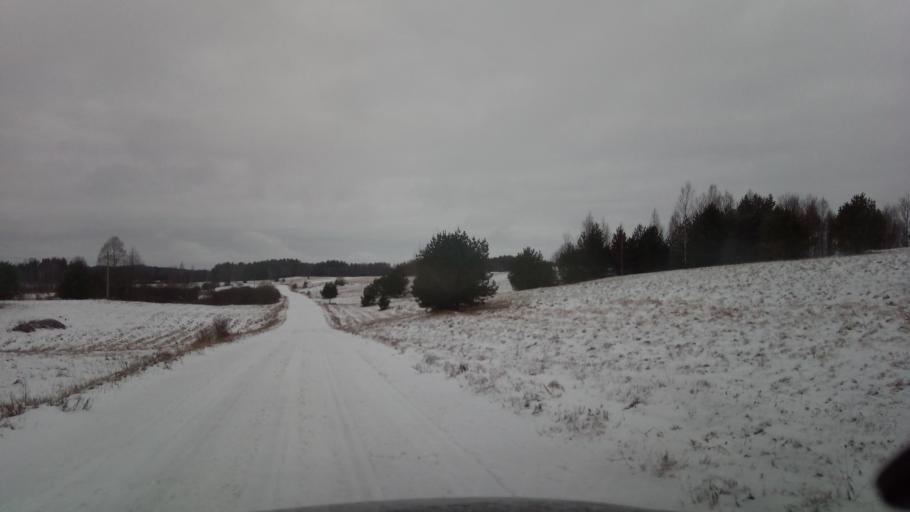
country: LT
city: Zarasai
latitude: 55.6849
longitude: 26.1041
